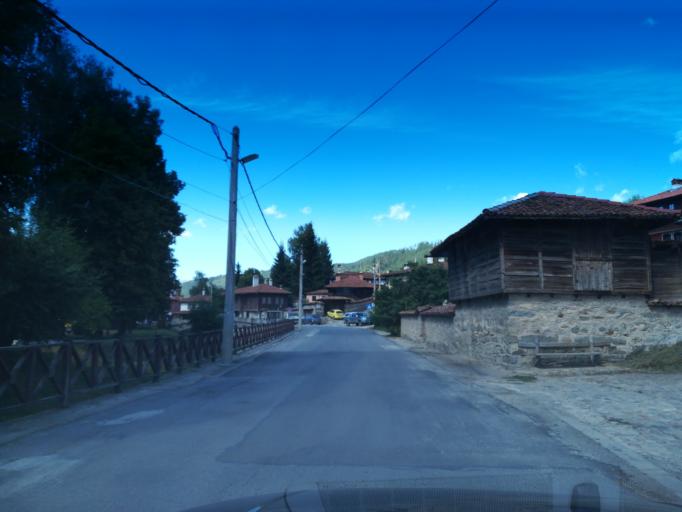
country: BG
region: Sofiya
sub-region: Obshtina Koprivshtitsa
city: Koprivshtitsa
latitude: 42.6388
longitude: 24.3596
